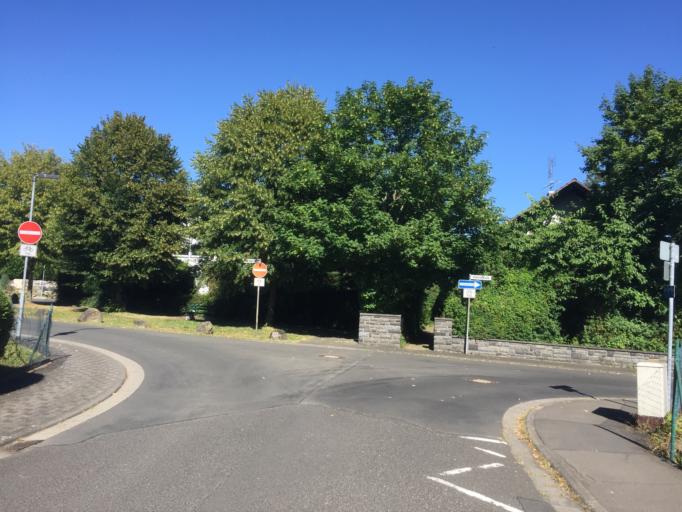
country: DE
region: Hesse
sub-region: Regierungsbezirk Giessen
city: Giessen
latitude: 50.5433
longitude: 8.7211
